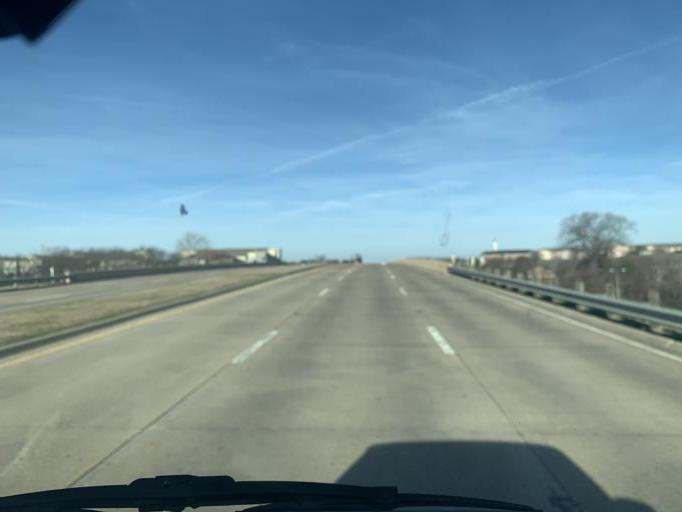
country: US
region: Texas
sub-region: Dallas County
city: Cedar Hill
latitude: 32.6018
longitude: -96.9463
